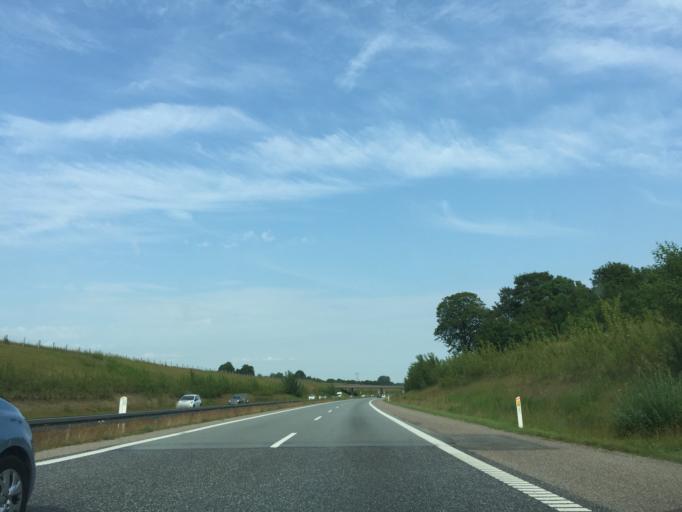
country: DK
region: Central Jutland
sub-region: Arhus Kommune
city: Lystrup
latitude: 56.2203
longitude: 10.1930
